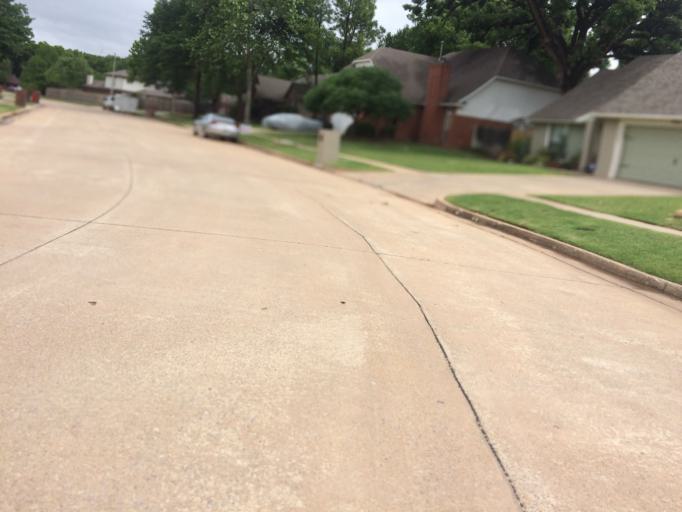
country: US
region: Oklahoma
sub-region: Cleveland County
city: Norman
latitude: 35.1834
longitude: -97.4538
